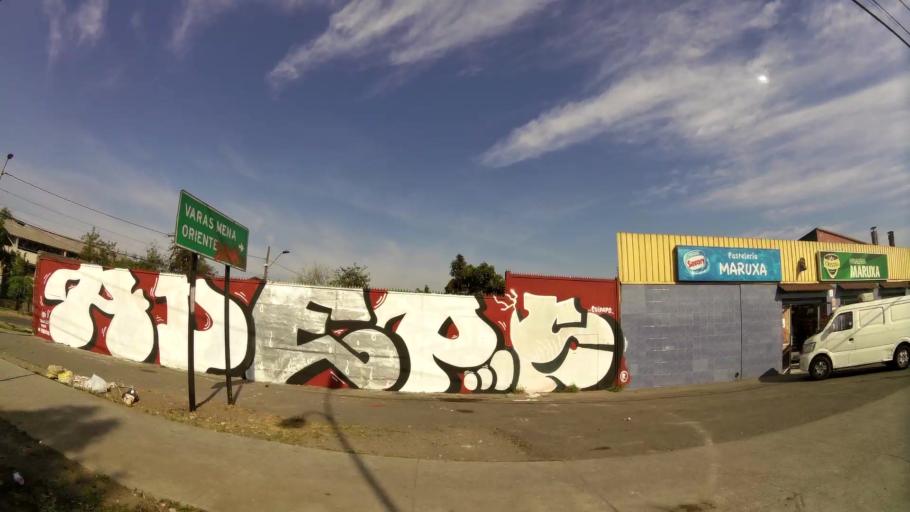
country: CL
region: Santiago Metropolitan
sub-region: Provincia de Santiago
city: Santiago
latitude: -33.5140
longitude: -70.6373
